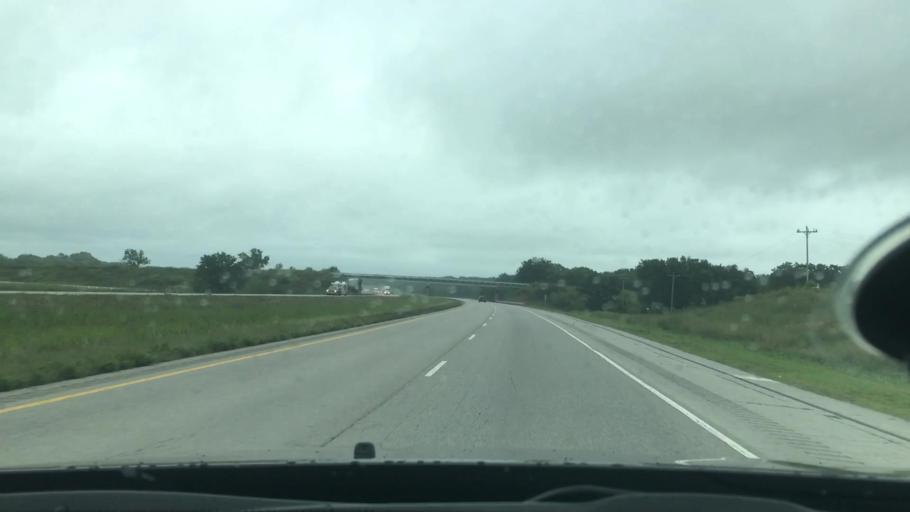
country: US
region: Oklahoma
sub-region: Okfuskee County
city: Boley
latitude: 35.3859
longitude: -96.4269
